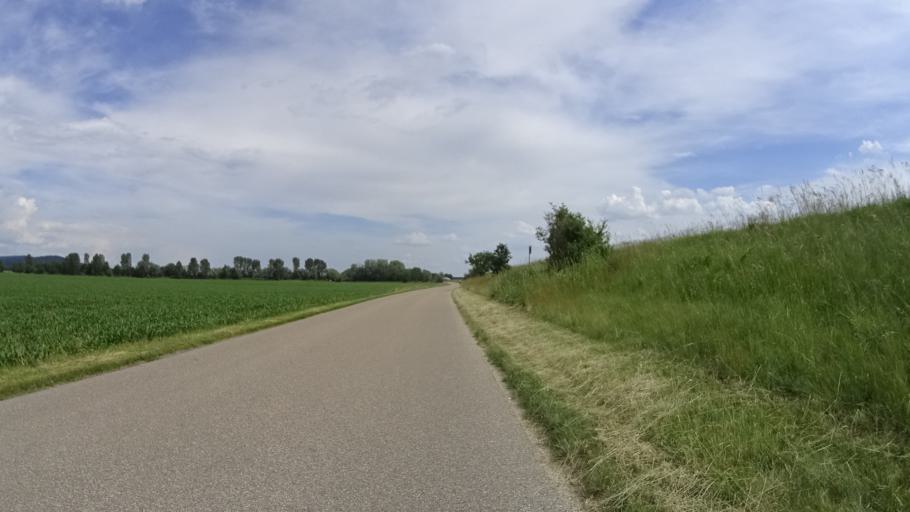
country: DE
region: Bavaria
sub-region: Upper Palatinate
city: Wiesent
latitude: 49.0107
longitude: 12.3290
